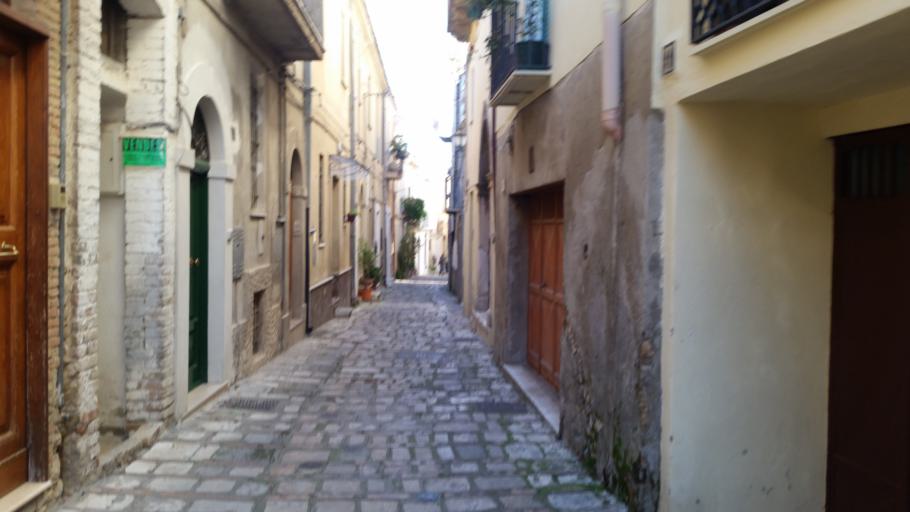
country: IT
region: Basilicate
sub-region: Provincia di Matera
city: Tricarico
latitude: 40.6214
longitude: 16.1449
